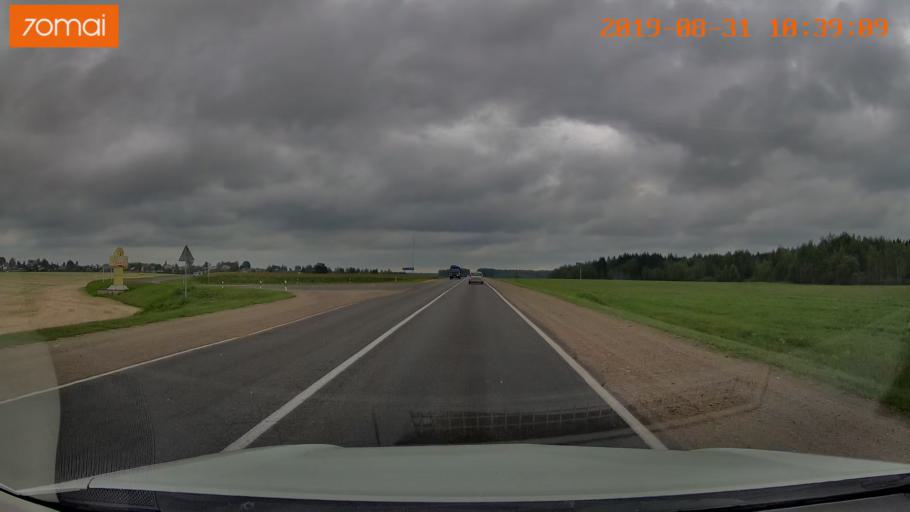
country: BY
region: Mogilev
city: Palykavichy Pyershyya
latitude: 53.9702
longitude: 30.2670
